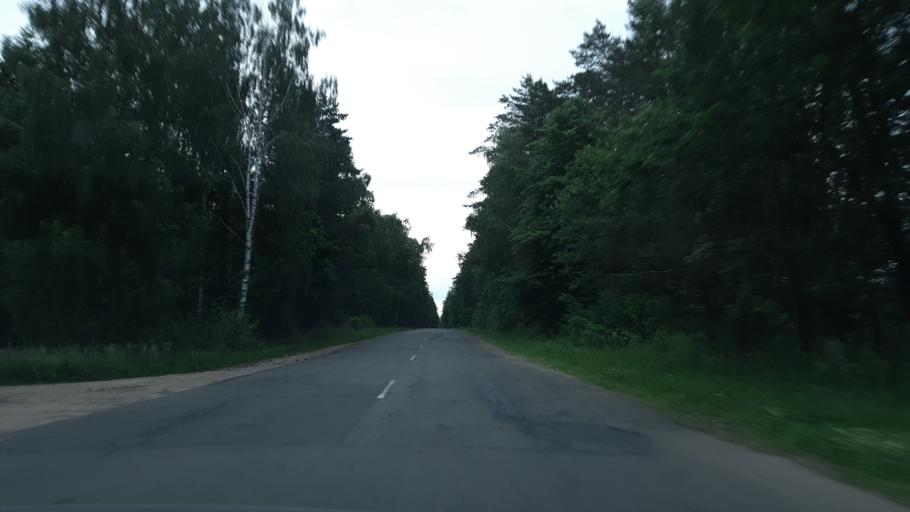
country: BY
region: Minsk
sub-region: Smalyavitski Rayon
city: Oktjabr'skij
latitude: 54.1113
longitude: 28.1959
